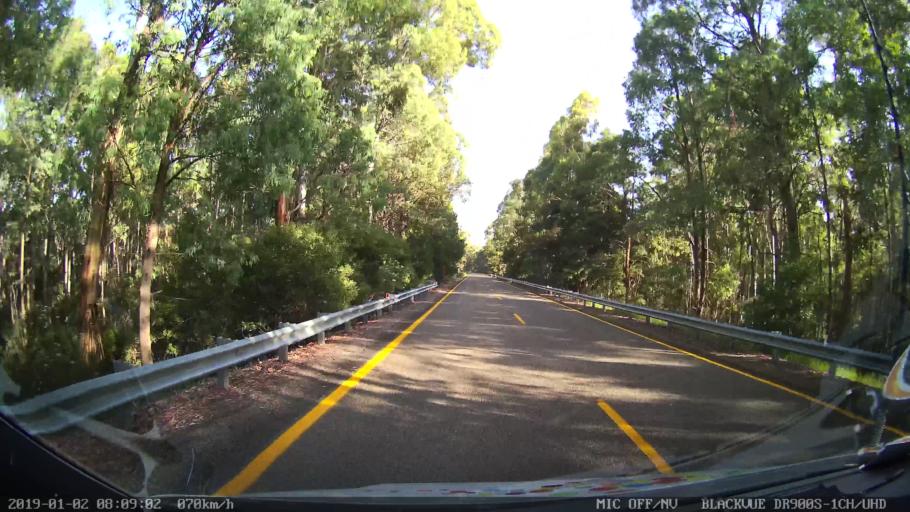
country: AU
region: New South Wales
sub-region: Tumut Shire
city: Tumut
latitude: -35.6110
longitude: 148.3814
